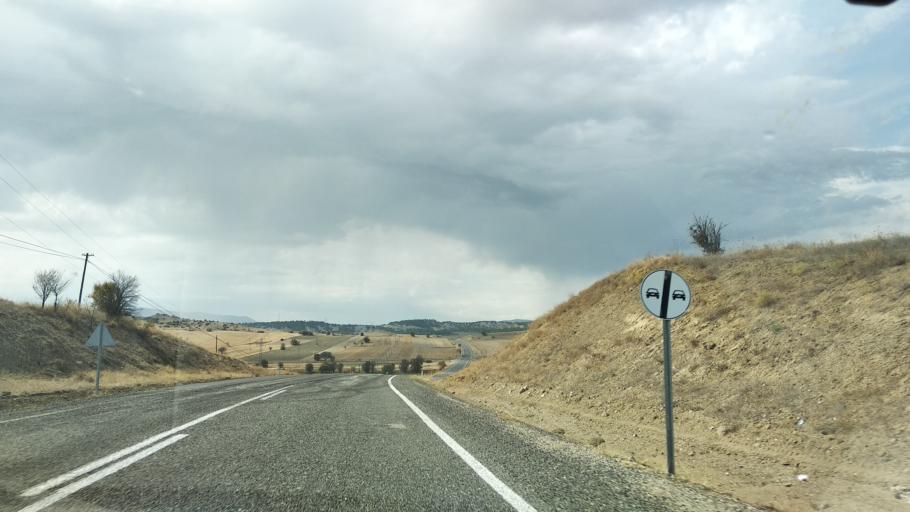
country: TR
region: Bolu
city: Seben
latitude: 40.3715
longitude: 31.5094
